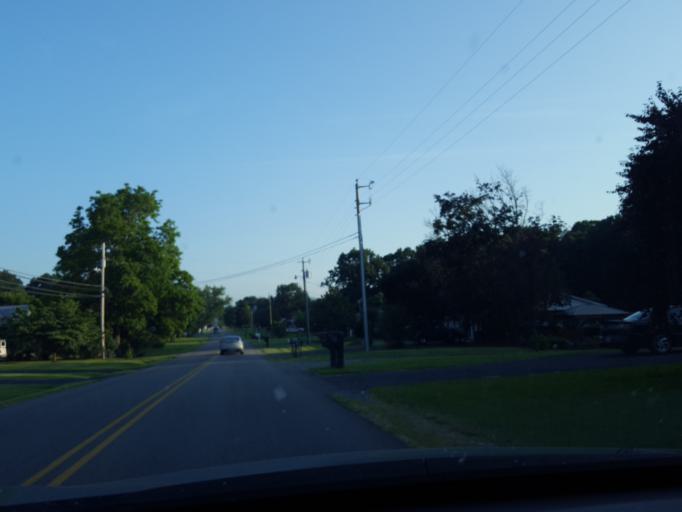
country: US
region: Virginia
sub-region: Augusta County
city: Lyndhurst
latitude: 38.0238
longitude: -78.9457
